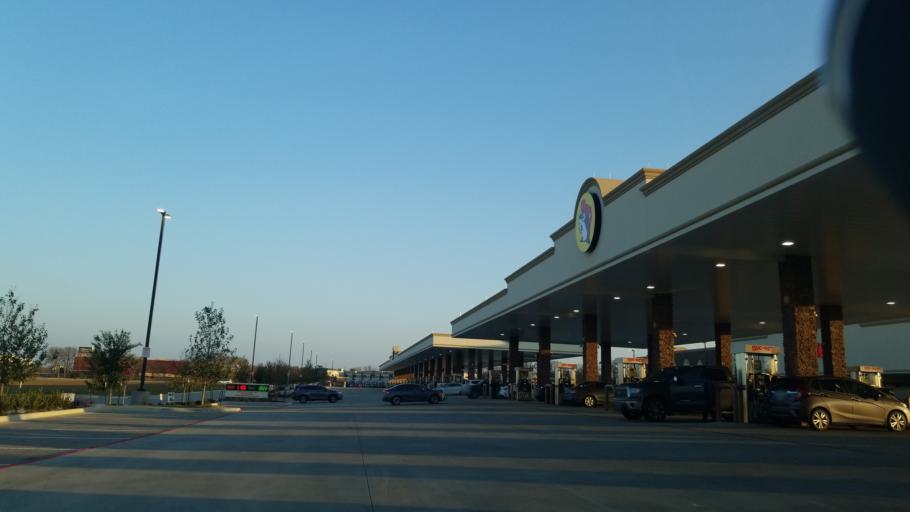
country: US
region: Texas
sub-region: Denton County
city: Denton
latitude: 33.1803
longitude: -97.1028
